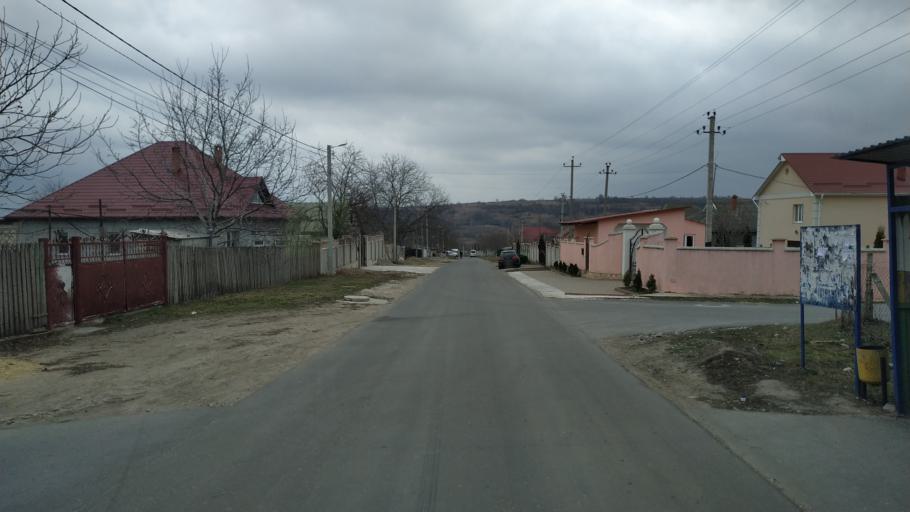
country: MD
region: Laloveni
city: Ialoveni
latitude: 46.9295
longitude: 28.7776
